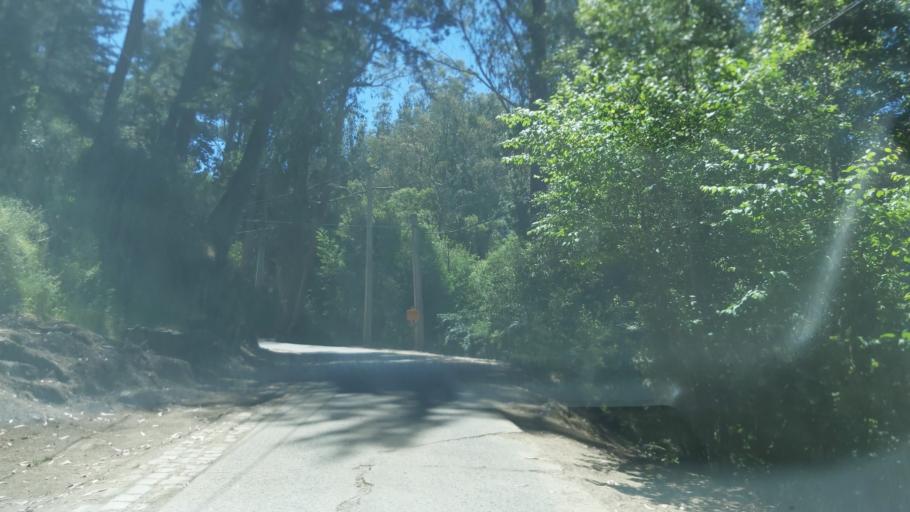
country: CL
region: Maule
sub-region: Provincia de Talca
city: Constitucion
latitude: -35.3245
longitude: -72.4134
